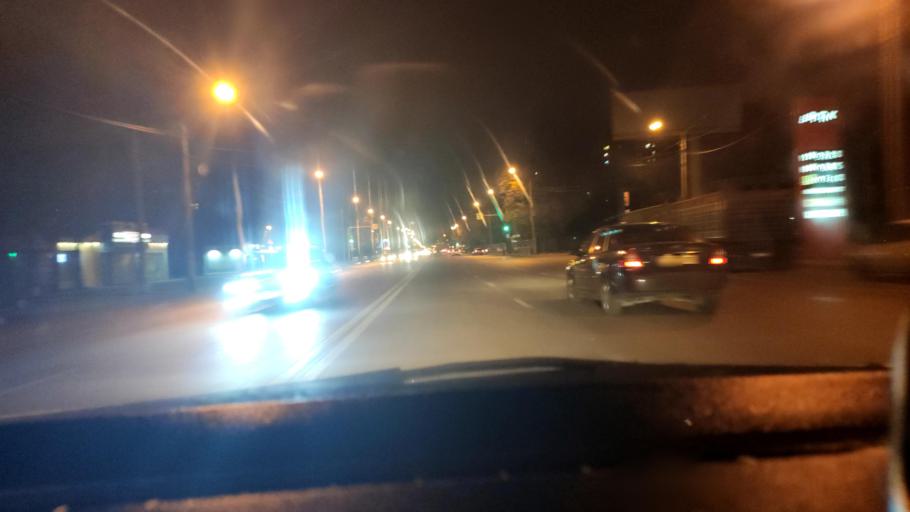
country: RU
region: Voronezj
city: Voronezh
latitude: 51.6690
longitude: 39.1664
